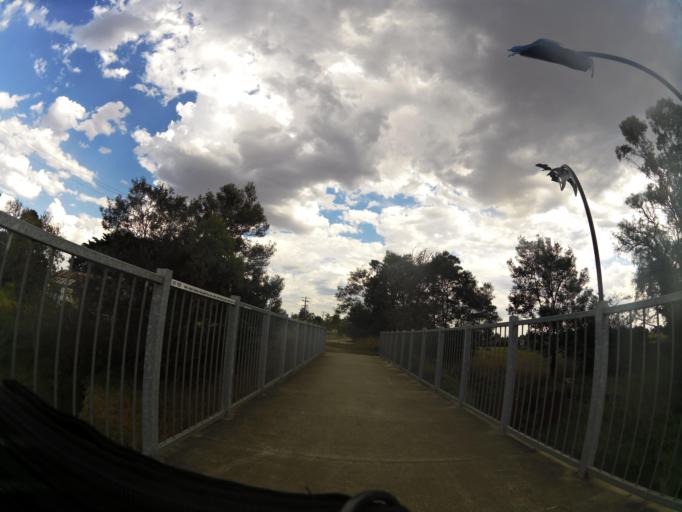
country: AU
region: Victoria
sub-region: Wellington
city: Heyfield
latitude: -38.0101
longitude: 146.6967
